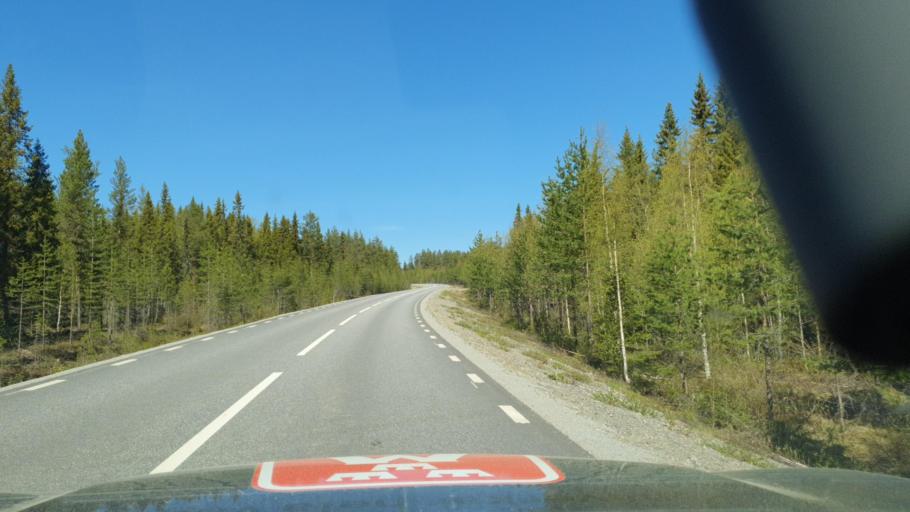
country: SE
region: Vaesterbotten
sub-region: Lycksele Kommun
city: Lycksele
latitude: 64.0198
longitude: 18.4514
